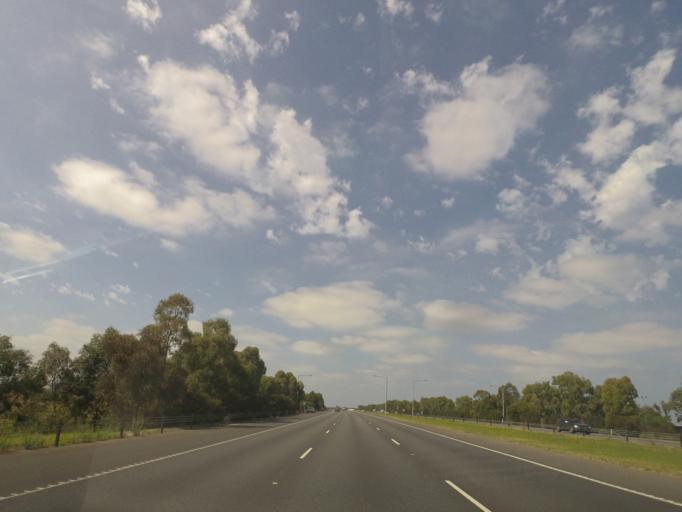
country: AU
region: Victoria
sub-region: Frankston
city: Sandhurst
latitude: -38.0387
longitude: 145.1883
